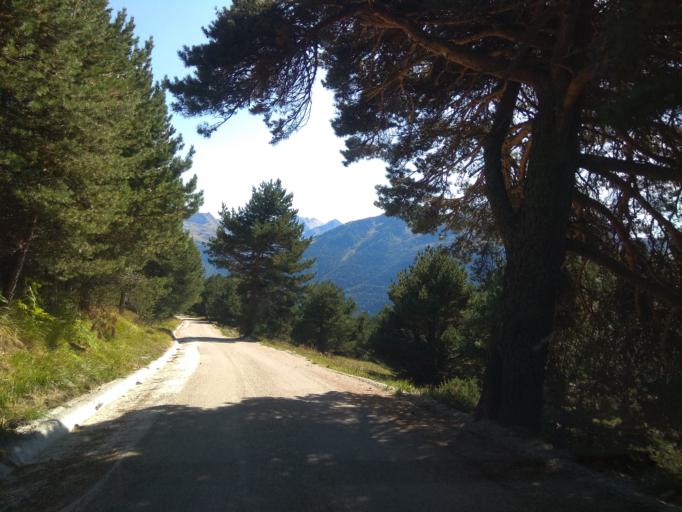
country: ES
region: Catalonia
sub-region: Provincia de Lleida
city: Les
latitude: 42.7646
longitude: 0.7136
